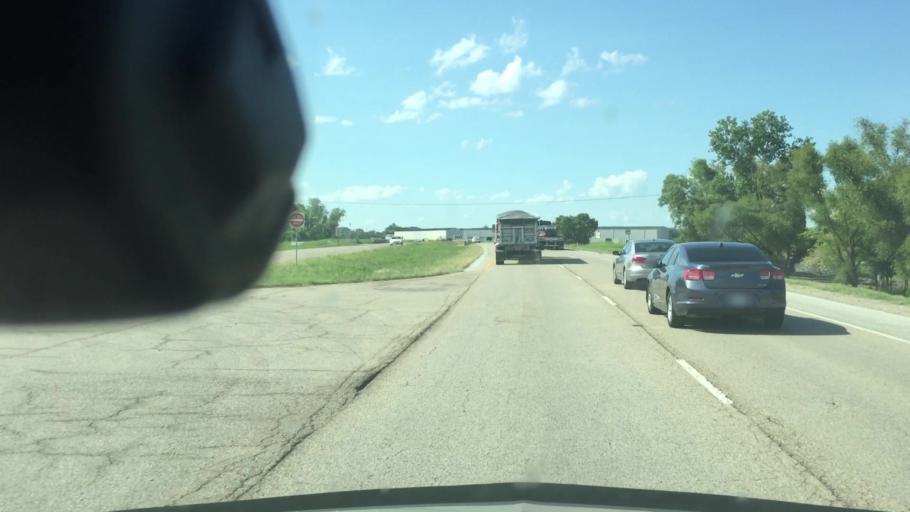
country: US
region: Illinois
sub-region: Saint Clair County
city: East Saint Louis
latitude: 38.6548
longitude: -90.1338
